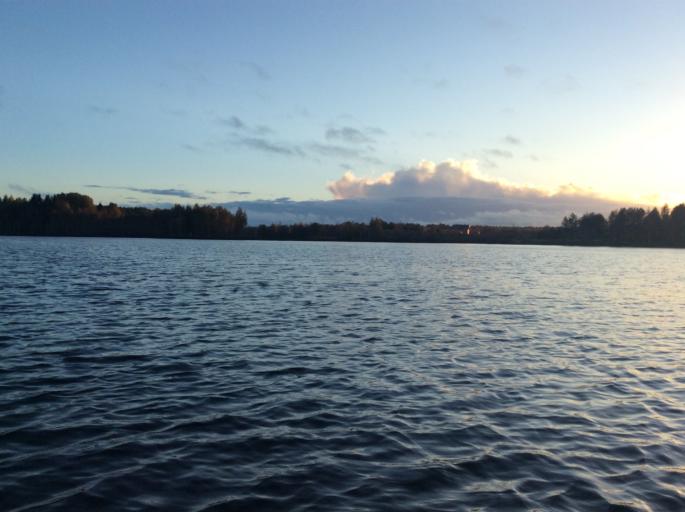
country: RU
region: Vologda
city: Ferapontovo
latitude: 59.9720
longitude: 38.6230
